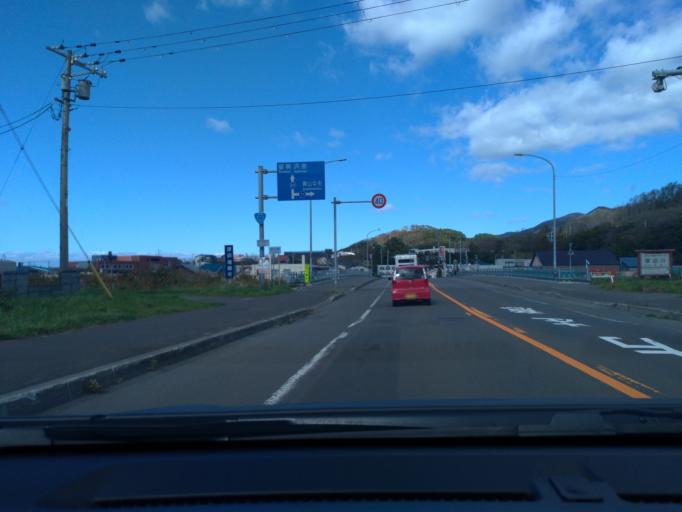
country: JP
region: Hokkaido
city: Ishikari
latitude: 43.3979
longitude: 141.4367
